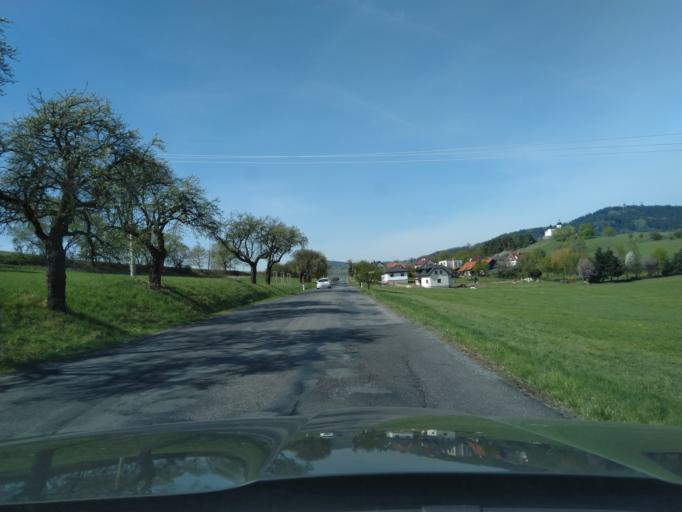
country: CZ
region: Plzensky
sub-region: Okres Klatovy
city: Susice
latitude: 49.2358
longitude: 13.5345
